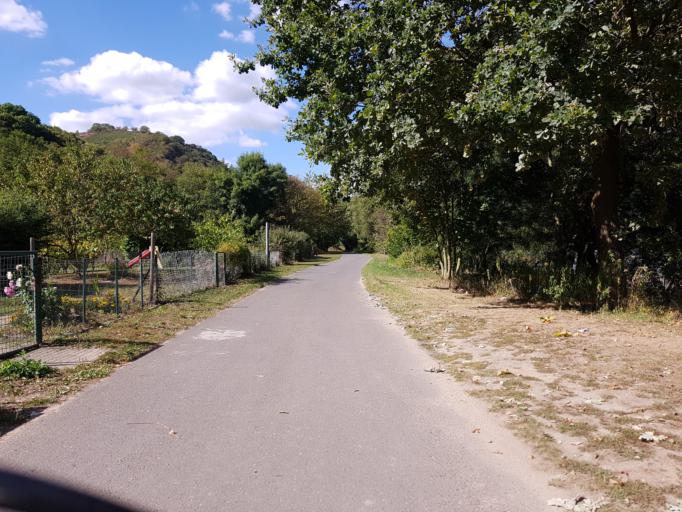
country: DE
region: Rheinland-Pfalz
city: Oberdiebach
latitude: 50.0446
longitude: 7.7861
